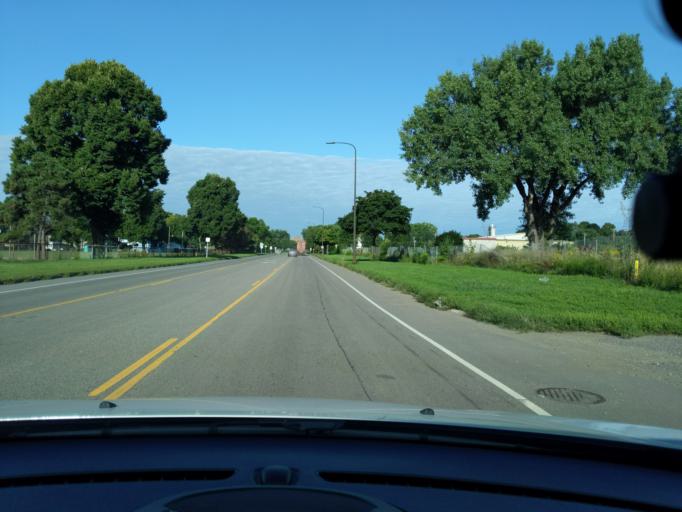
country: US
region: Minnesota
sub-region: Ramsey County
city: Saint Paul
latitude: 44.9648
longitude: -93.1289
